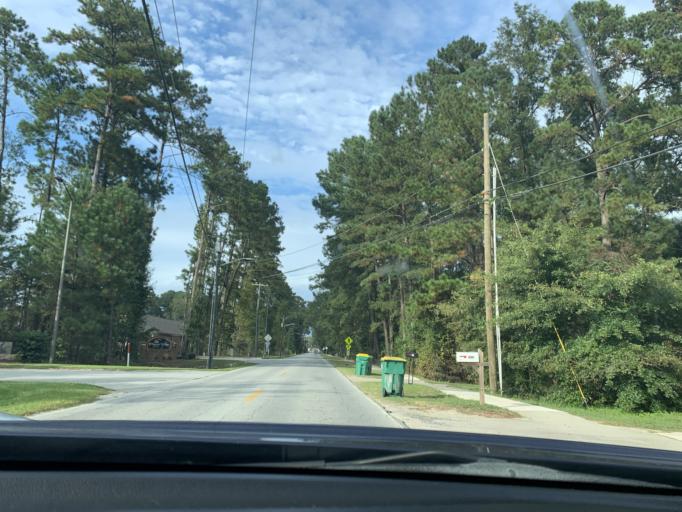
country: US
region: Georgia
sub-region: Chatham County
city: Pooler
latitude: 32.1095
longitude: -81.2511
